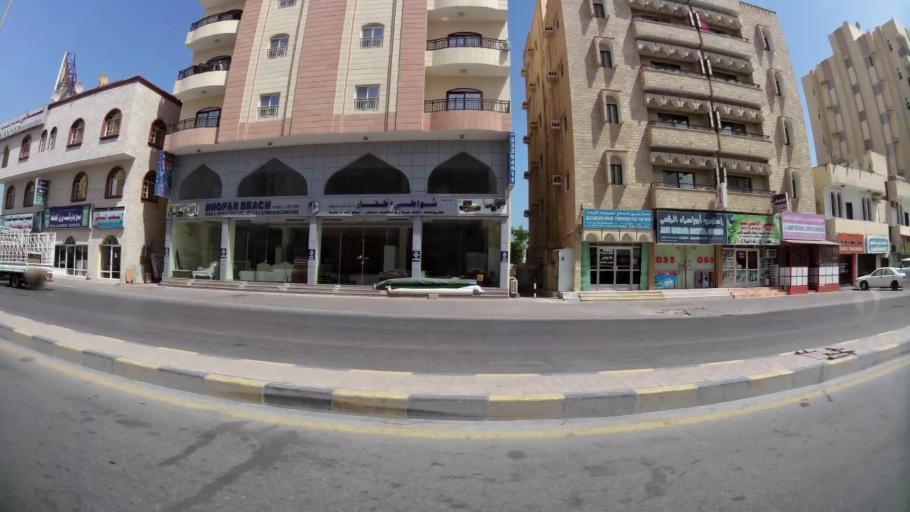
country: OM
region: Zufar
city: Salalah
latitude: 17.0130
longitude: 54.0856
